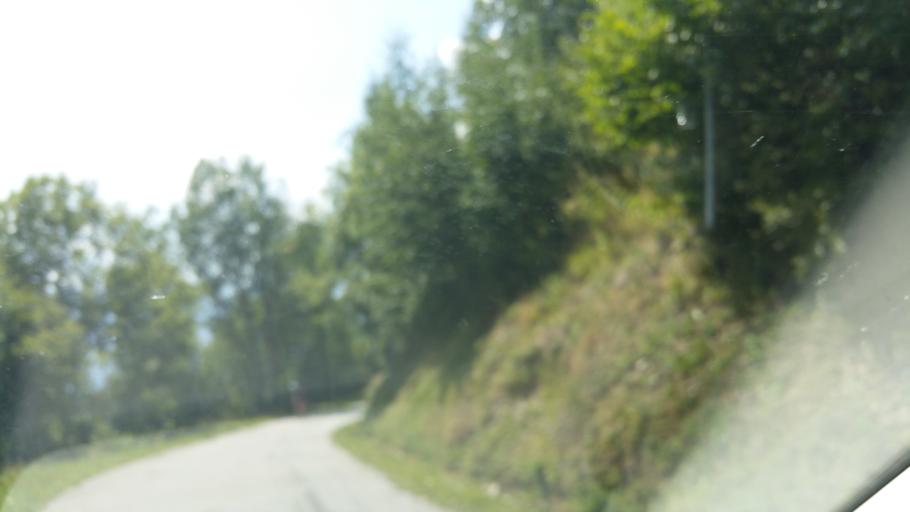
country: FR
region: Rhone-Alpes
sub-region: Departement de la Savoie
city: La Chambre
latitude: 45.4074
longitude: 6.3325
